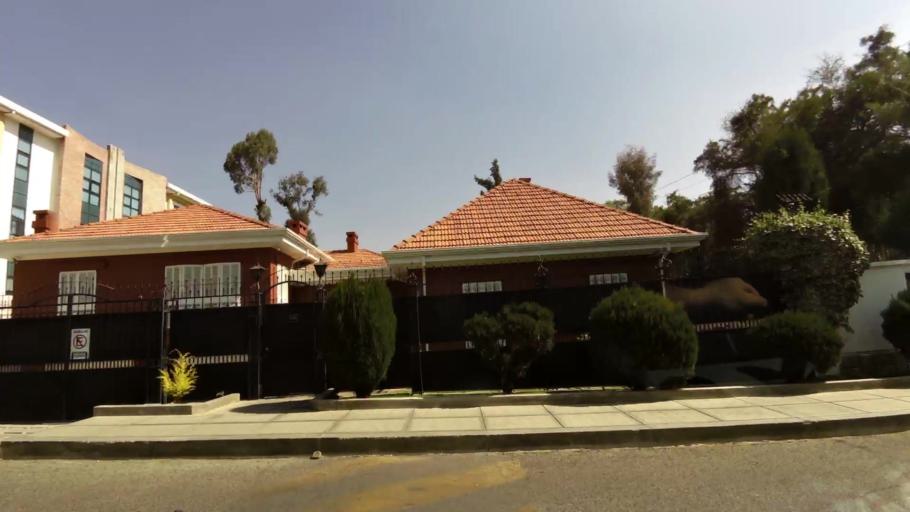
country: BO
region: La Paz
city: La Paz
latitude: -16.5423
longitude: -68.0880
